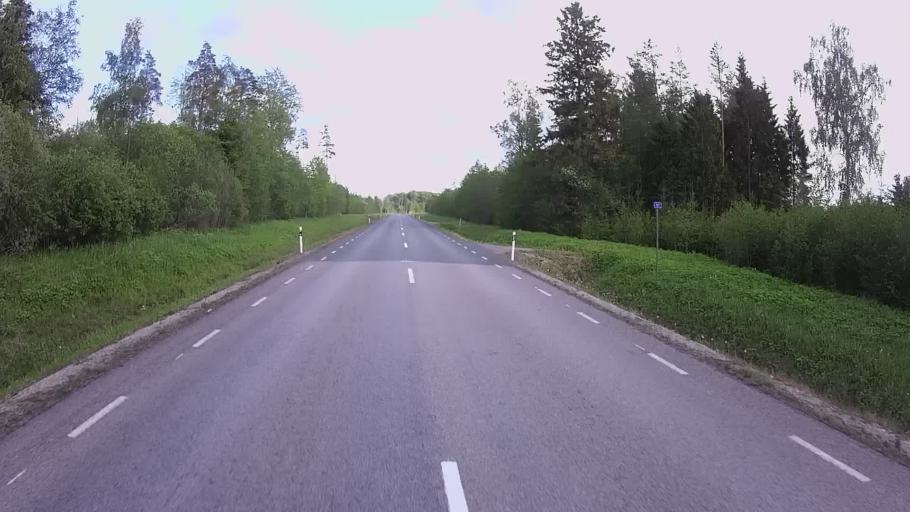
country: EE
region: Jogevamaa
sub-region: Mustvee linn
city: Mustvee
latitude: 59.0583
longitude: 27.0082
